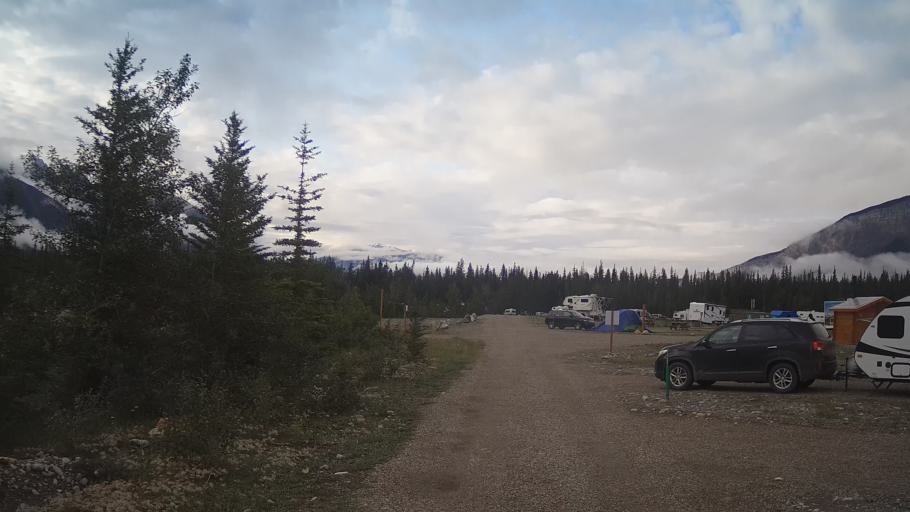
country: CA
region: Alberta
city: Jasper Park Lodge
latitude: 53.0175
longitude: -118.0844
